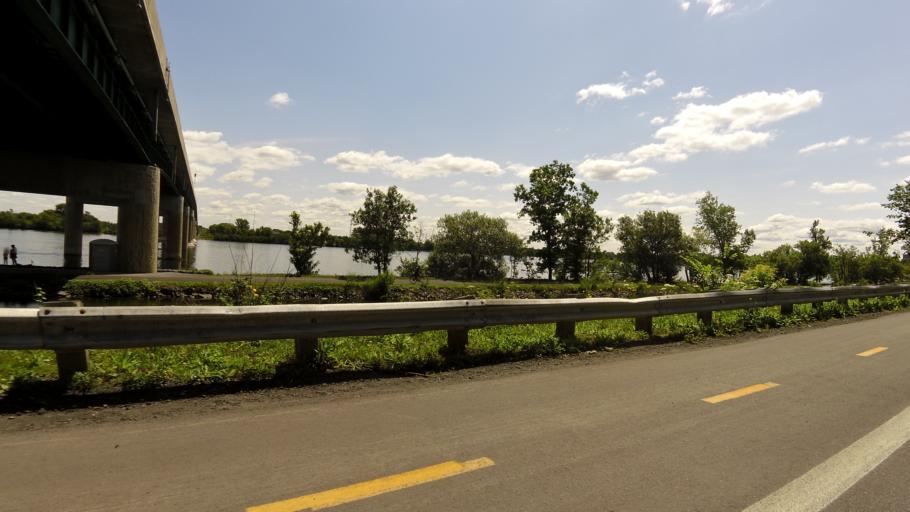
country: CA
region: Quebec
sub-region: Monteregie
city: Saint-Jean-sur-Richelieu
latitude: 45.3266
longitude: -73.2634
